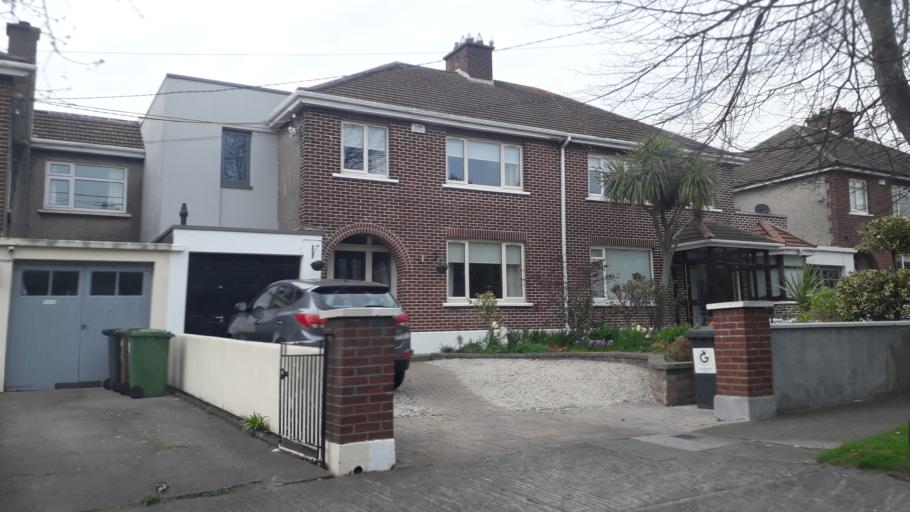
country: IE
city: Donnycarney
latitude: 53.3649
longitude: -6.2079
